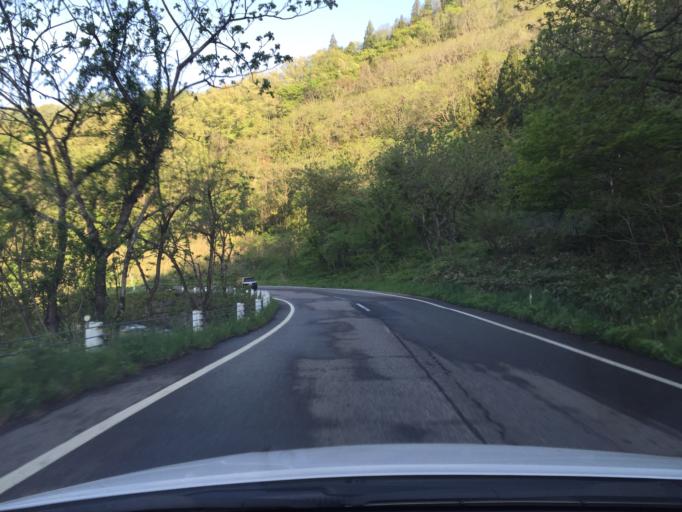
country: JP
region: Fukushima
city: Kitakata
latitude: 37.6608
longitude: 139.9518
